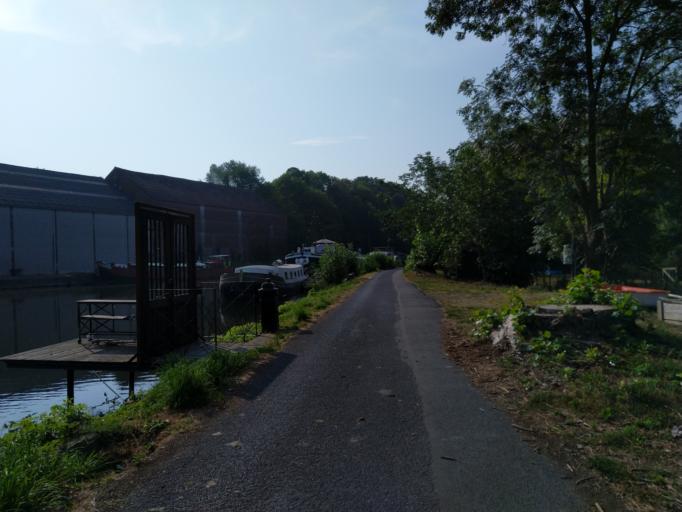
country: BE
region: Wallonia
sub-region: Province du Brabant Wallon
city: Ittre
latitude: 50.6057
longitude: 4.2279
